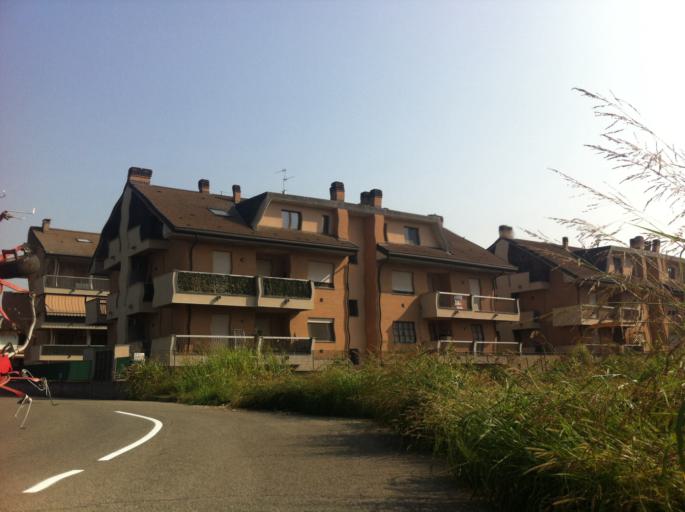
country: IT
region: Lombardy
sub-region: Provincia di Lodi
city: Quartiano
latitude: 45.3561
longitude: 9.4120
